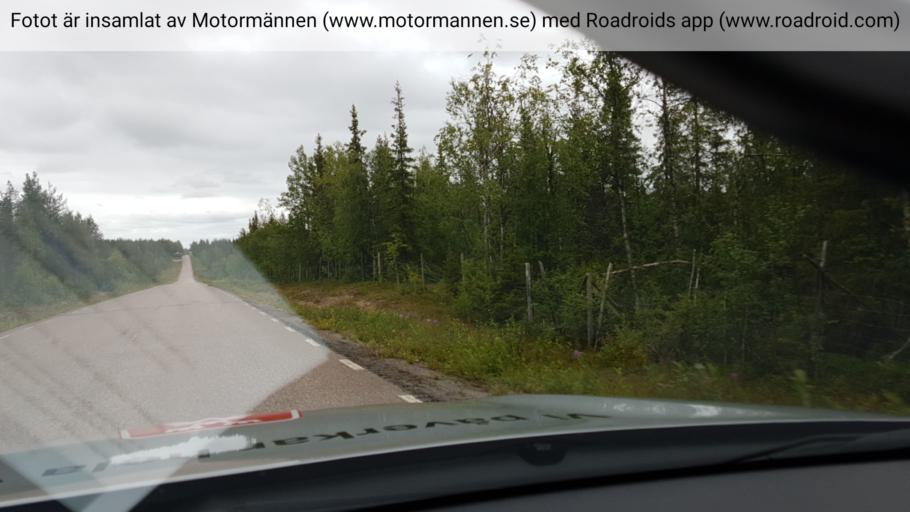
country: SE
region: Norrbotten
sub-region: Overkalix Kommun
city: OEverkalix
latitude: 67.0443
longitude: 22.0800
